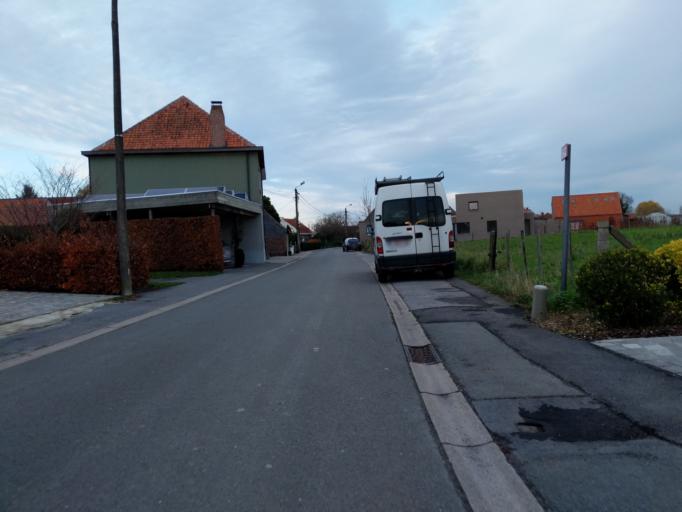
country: BE
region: Flanders
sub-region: Provincie West-Vlaanderen
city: Ruiselede
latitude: 51.0395
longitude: 3.3999
